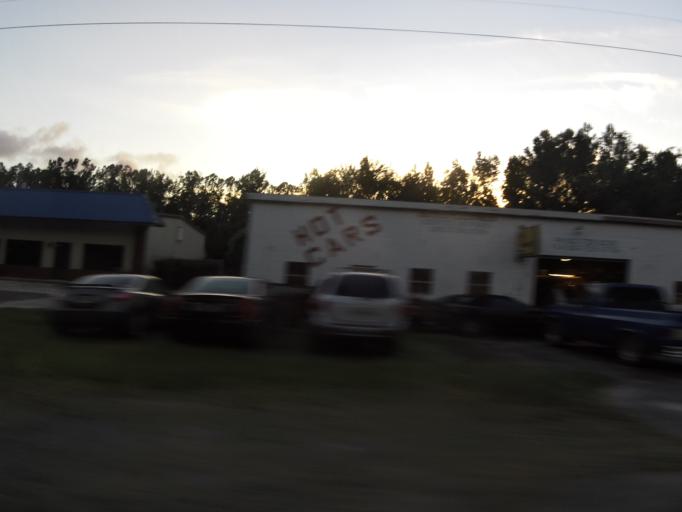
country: US
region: Georgia
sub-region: Camden County
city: Kingsland
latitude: 30.8242
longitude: -81.6951
